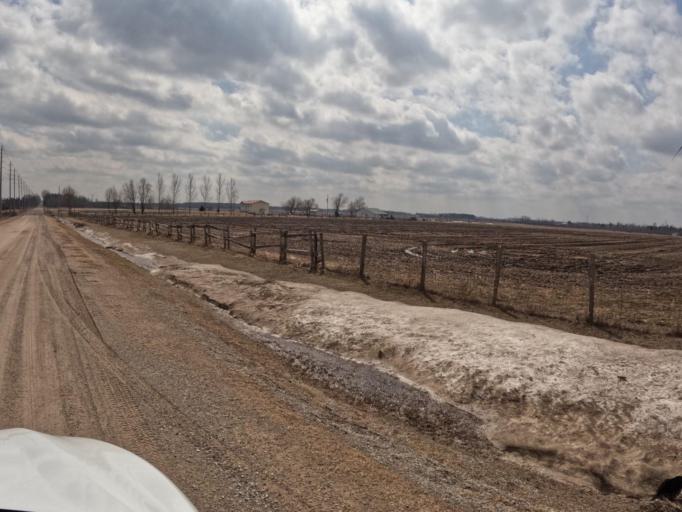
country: CA
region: Ontario
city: Shelburne
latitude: 44.0283
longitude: -80.3147
